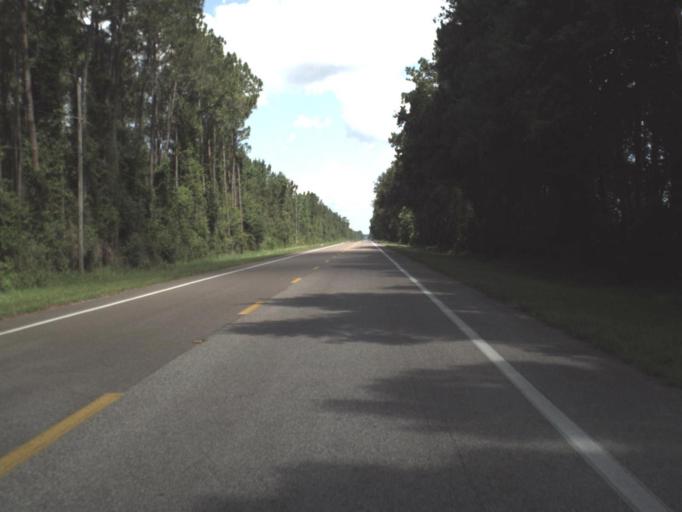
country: US
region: Florida
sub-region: Putnam County
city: Crescent City
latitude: 29.5465
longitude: -81.5285
